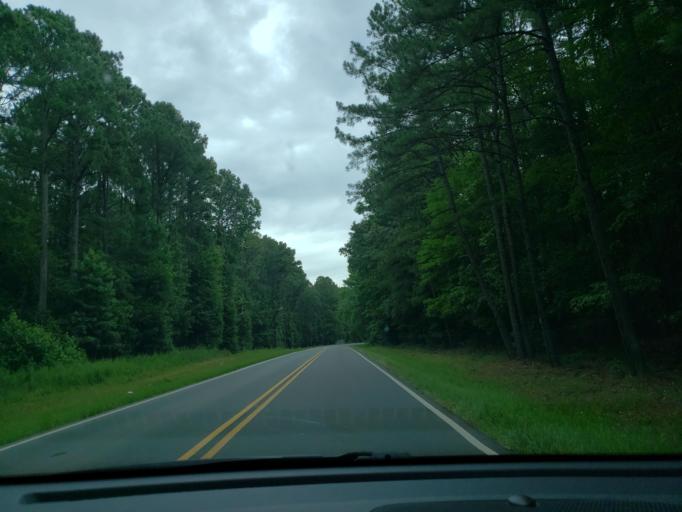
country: US
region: North Carolina
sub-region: Chatham County
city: Fearrington Village
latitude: 35.7107
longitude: -79.0145
